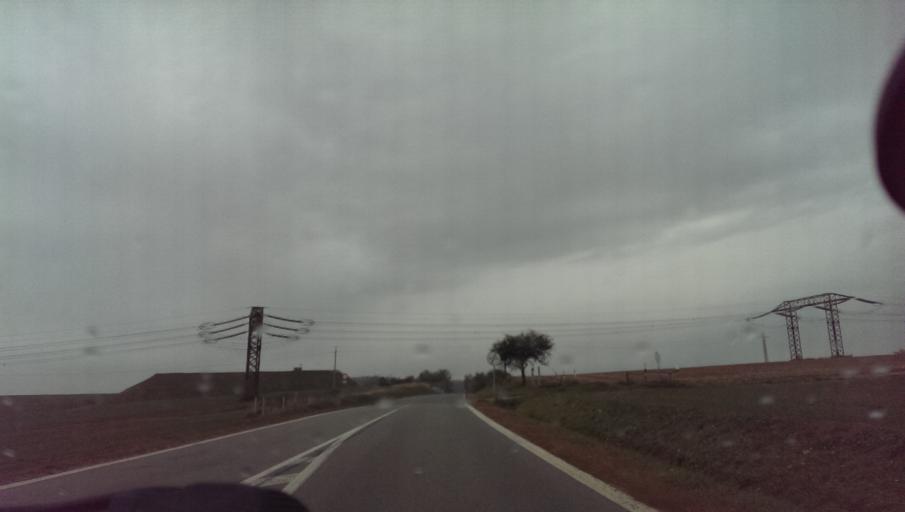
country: CZ
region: South Moravian
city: Moravany
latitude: 49.1454
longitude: 16.5605
